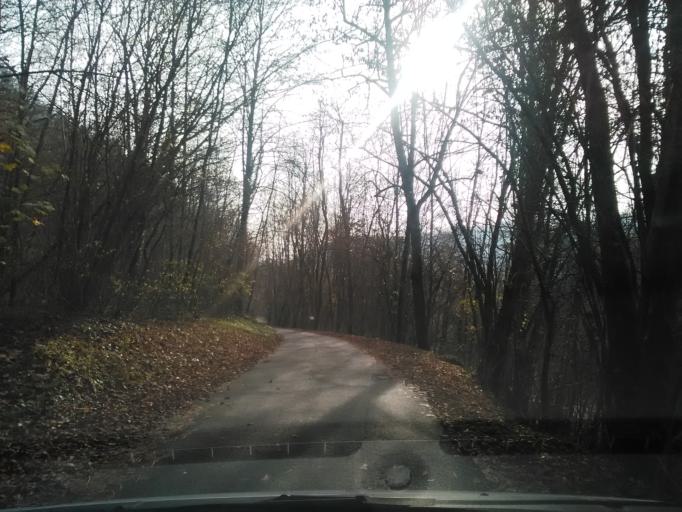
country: IT
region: Piedmont
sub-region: Provincia di Vercelli
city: Postua
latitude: 45.7055
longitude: 8.2365
